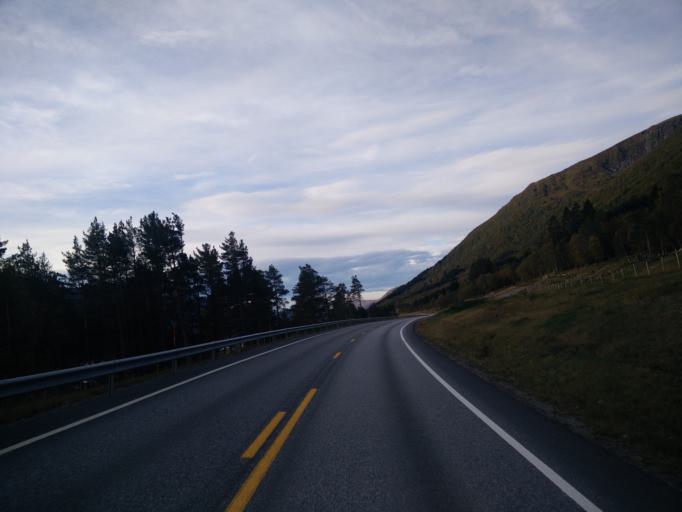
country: NO
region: More og Romsdal
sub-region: Gjemnes
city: Batnfjordsora
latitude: 62.9477
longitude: 7.7528
